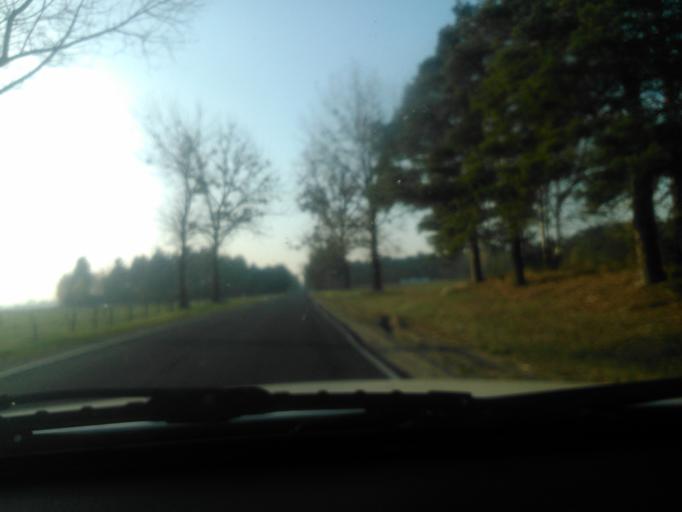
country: PL
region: Masovian Voivodeship
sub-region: Powiat ostrolecki
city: Czarnia
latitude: 53.3019
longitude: 21.0651
